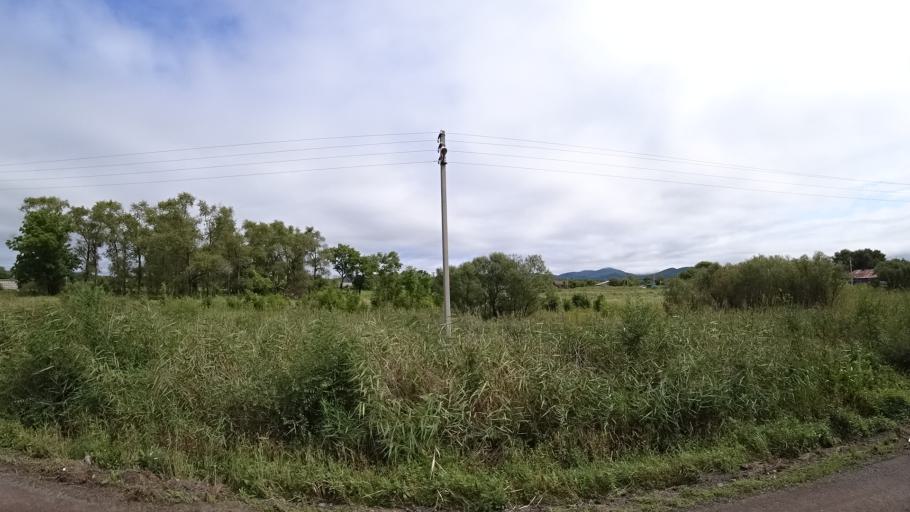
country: RU
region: Primorskiy
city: Monastyrishche
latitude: 44.1907
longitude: 132.4815
